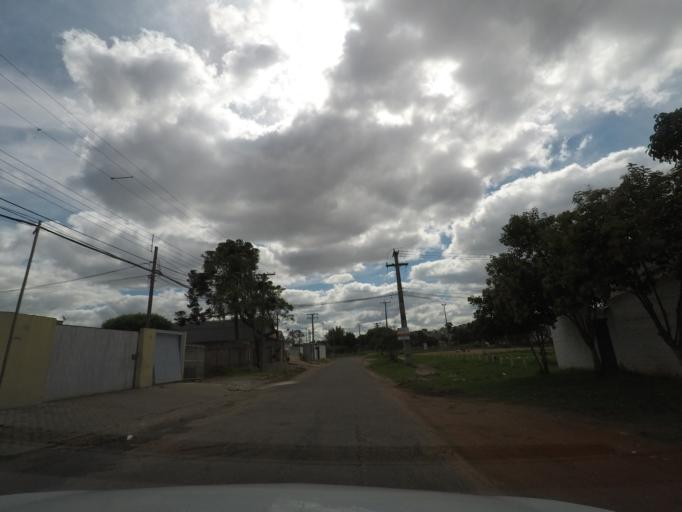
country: BR
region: Parana
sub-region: Sao Jose Dos Pinhais
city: Sao Jose dos Pinhais
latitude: -25.4891
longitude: -49.2325
